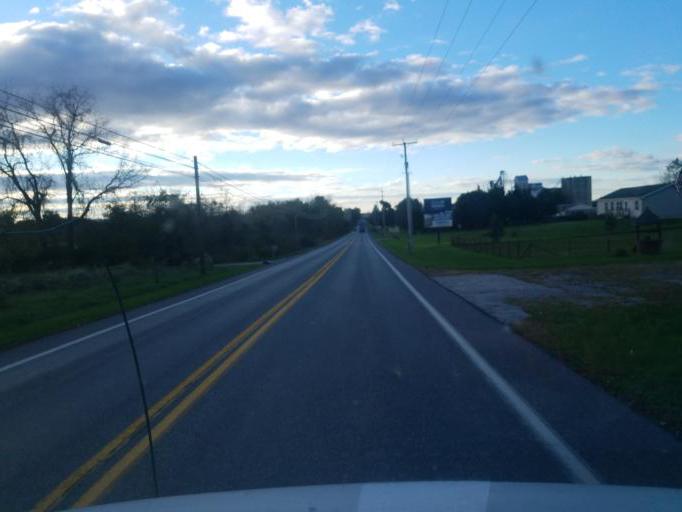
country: US
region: Pennsylvania
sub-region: Adams County
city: Lake Meade
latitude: 39.9350
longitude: -77.0608
